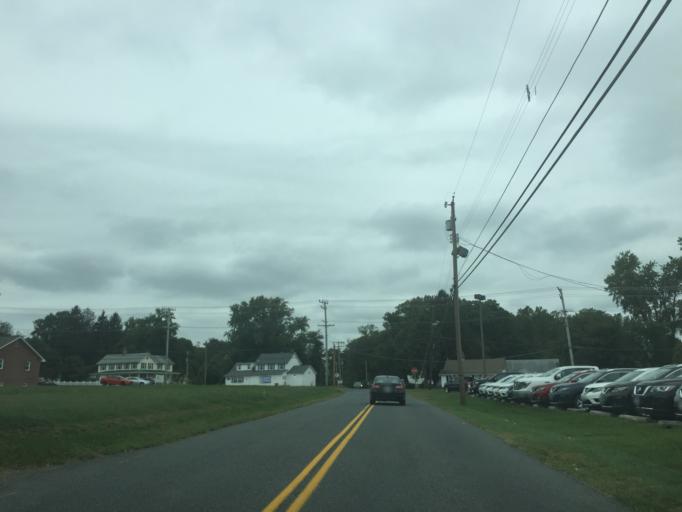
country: US
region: Maryland
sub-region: Harford County
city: Pleasant Hills
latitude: 39.5048
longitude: -76.3853
